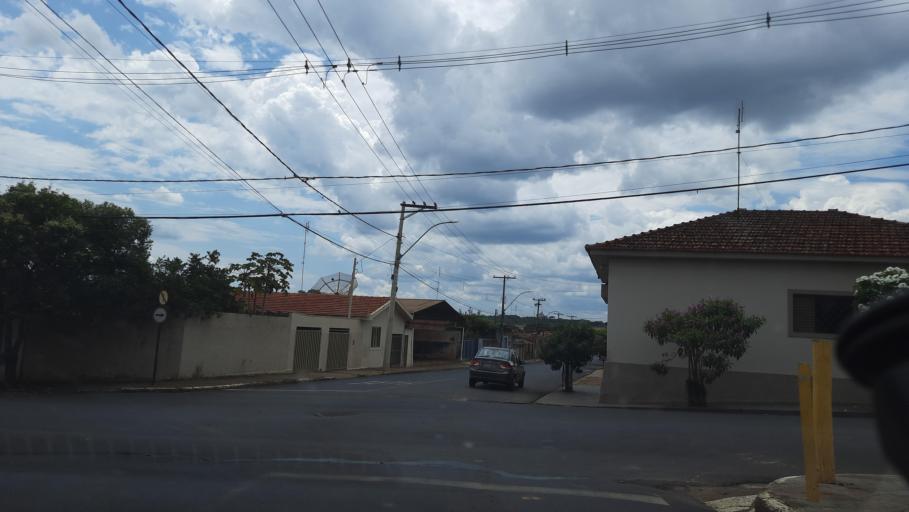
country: BR
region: Sao Paulo
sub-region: Cajuru
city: Cajuru
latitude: -21.2748
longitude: -47.2995
